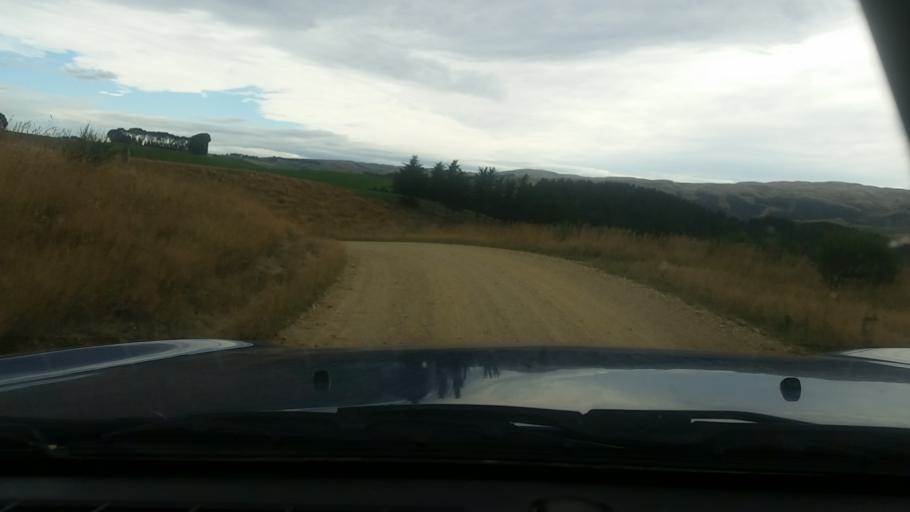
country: NZ
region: Otago
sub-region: Clutha District
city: Balclutha
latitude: -45.6966
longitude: 169.4962
